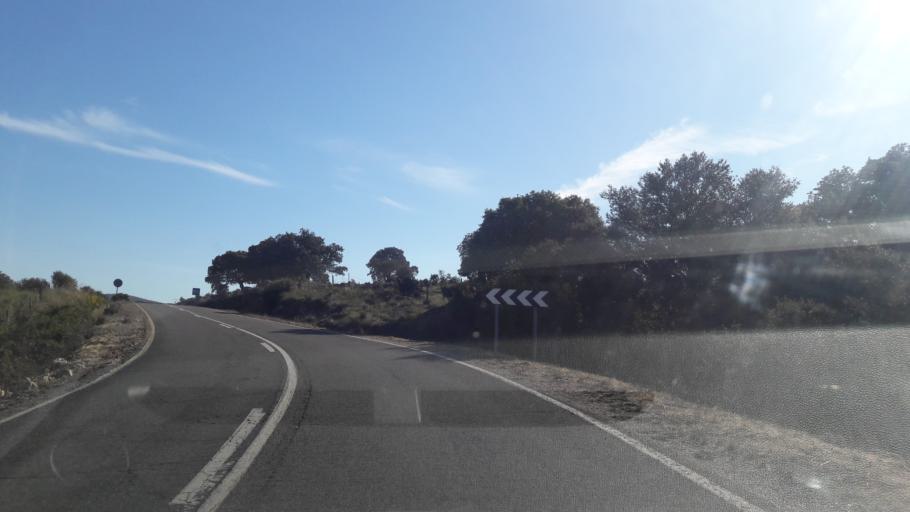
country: ES
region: Castille and Leon
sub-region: Provincia de Avila
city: Narrillos del Alamo
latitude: 40.5255
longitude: -5.4866
